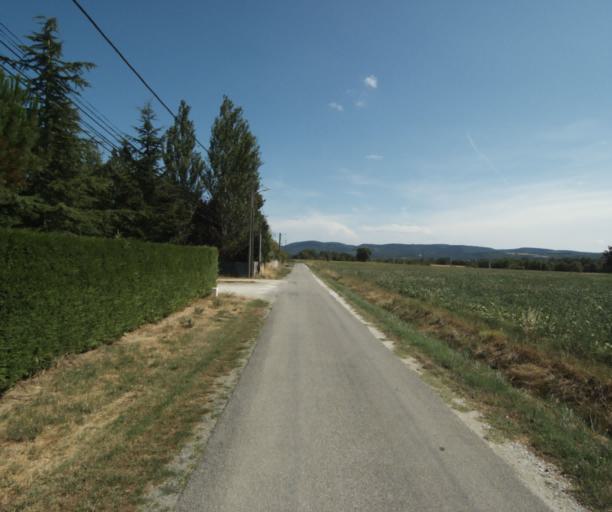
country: FR
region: Midi-Pyrenees
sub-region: Departement de la Haute-Garonne
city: Revel
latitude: 43.4836
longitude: 2.0053
